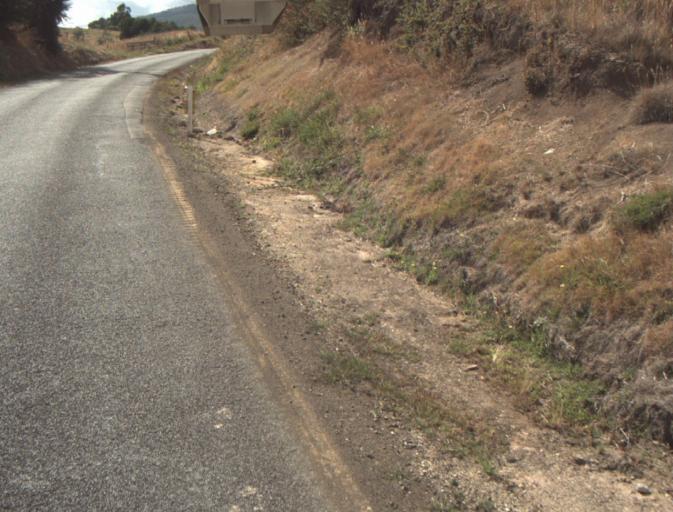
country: AU
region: Tasmania
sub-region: Launceston
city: Mayfield
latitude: -41.2574
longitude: 147.1979
